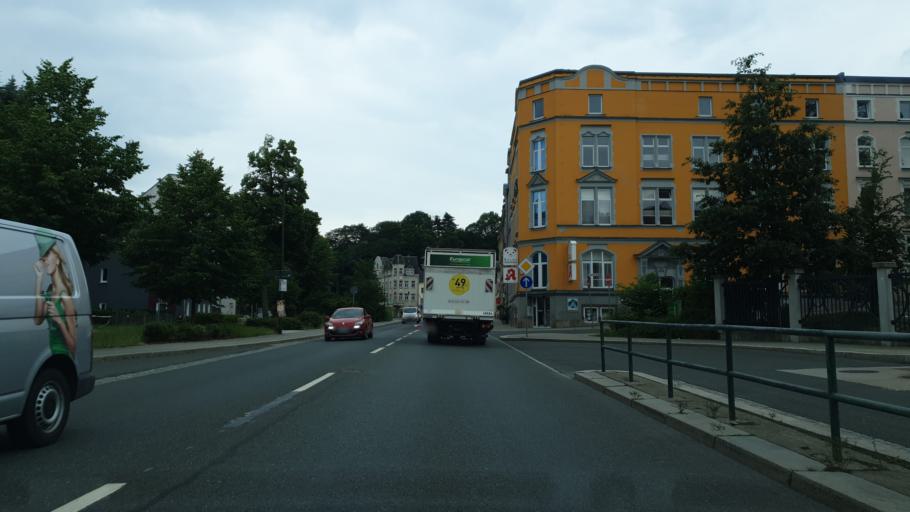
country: DE
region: Saxony
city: Auerbach
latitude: 50.5106
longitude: 12.3986
